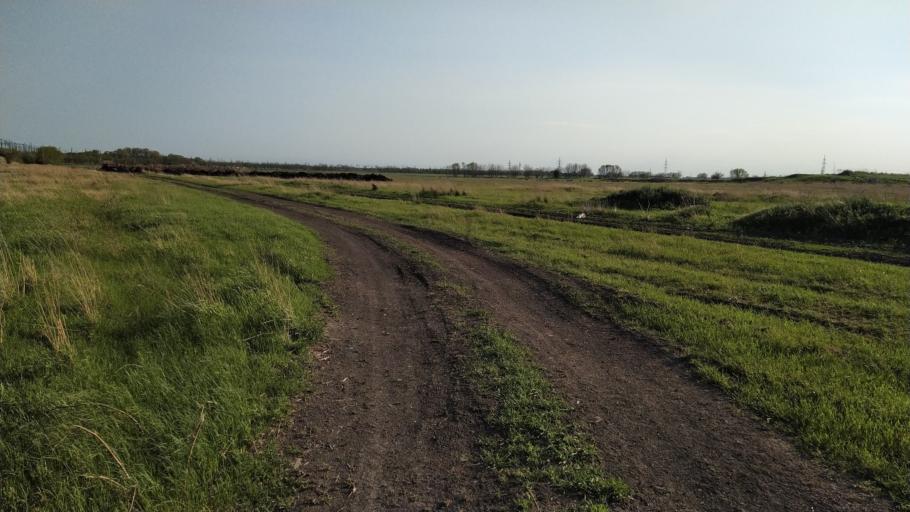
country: RU
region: Rostov
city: Bataysk
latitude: 47.0956
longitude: 39.7126
